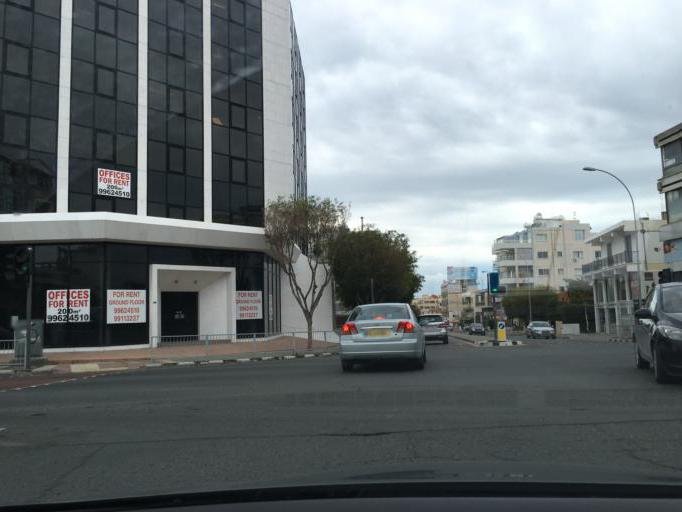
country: CY
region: Limassol
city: Limassol
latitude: 34.6878
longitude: 33.0444
